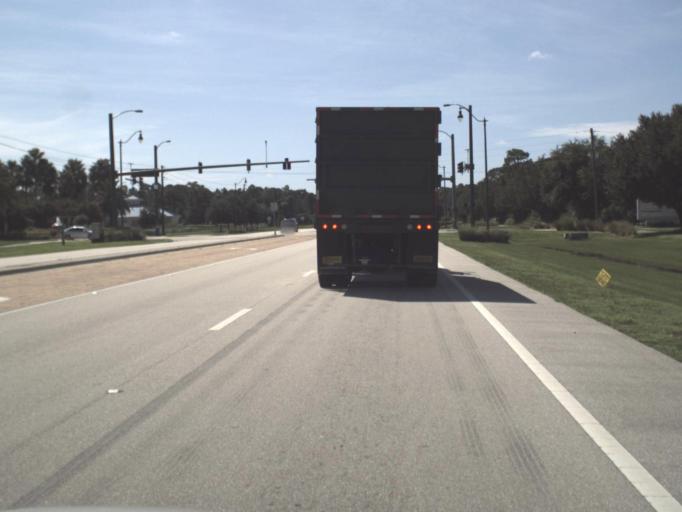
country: US
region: Florida
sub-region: Sarasota County
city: North Port
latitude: 27.0797
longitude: -82.1557
